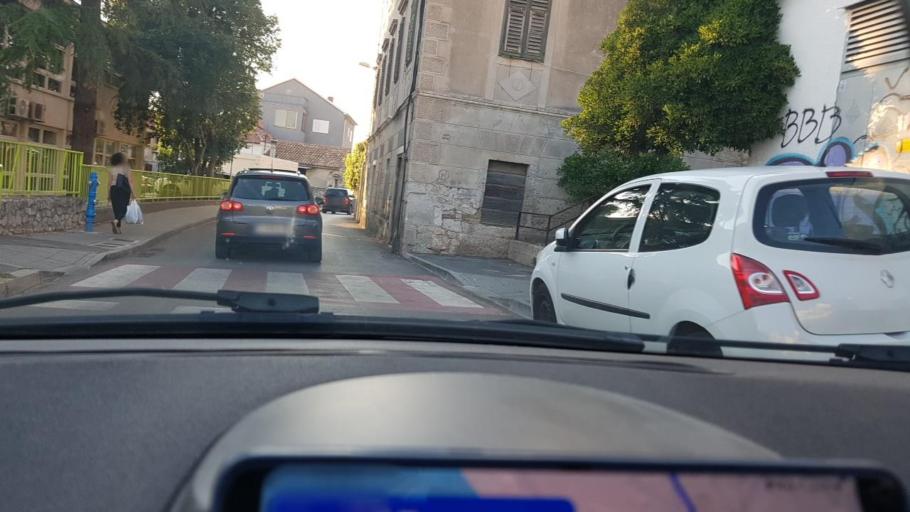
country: HR
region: Sibensko-Kniniska
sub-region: Grad Sibenik
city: Sibenik
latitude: 43.7406
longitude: 15.8897
